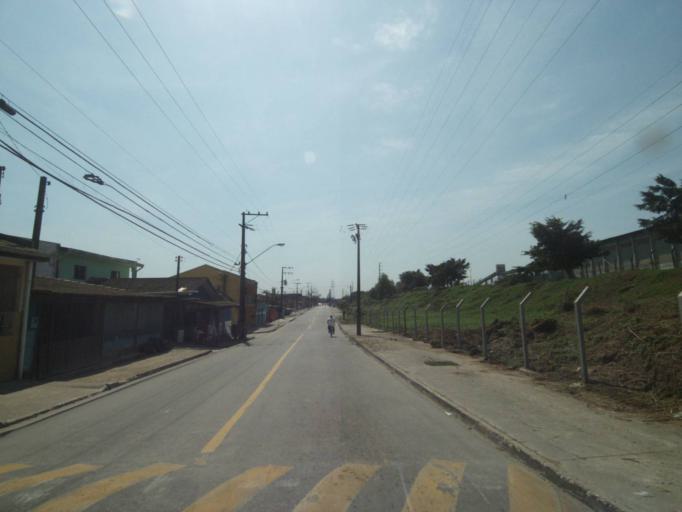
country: BR
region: Parana
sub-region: Paranagua
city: Paranagua
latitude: -25.5442
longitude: -48.5488
